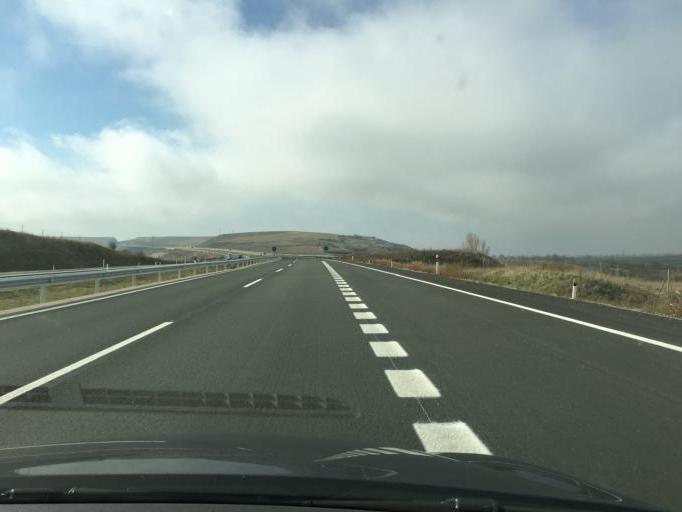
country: ES
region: Castille and Leon
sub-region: Provincia de Burgos
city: Villanueva de Teba
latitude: 42.6228
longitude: -3.1713
